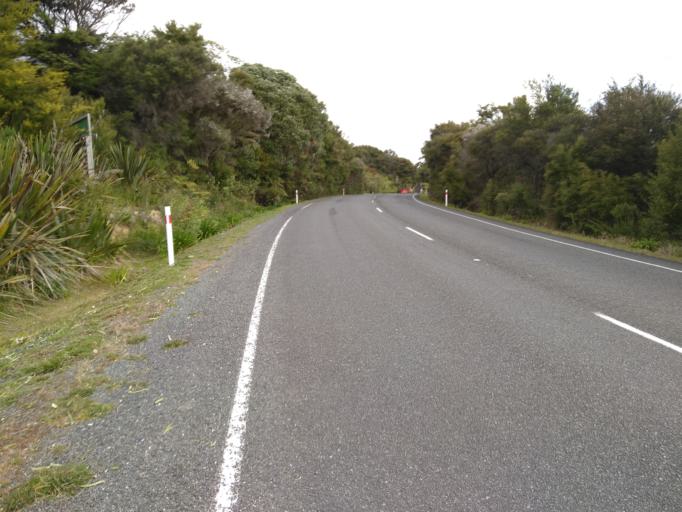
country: NZ
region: Northland
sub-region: Far North District
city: Paihia
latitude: -35.2825
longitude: 174.1473
